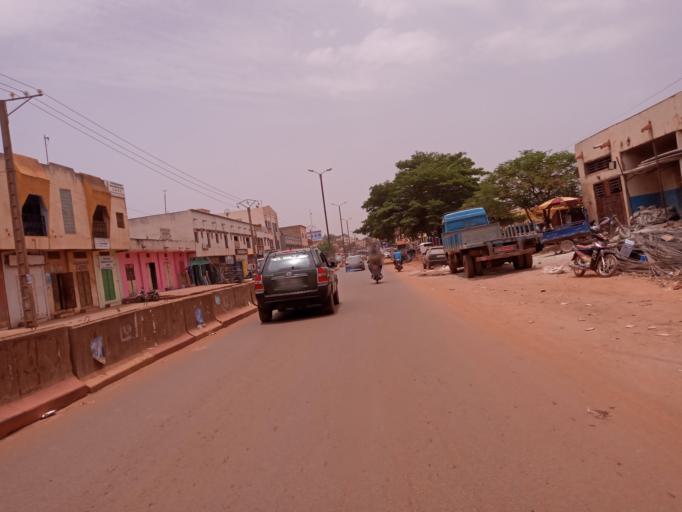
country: ML
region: Bamako
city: Bamako
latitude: 12.5862
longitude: -8.0224
